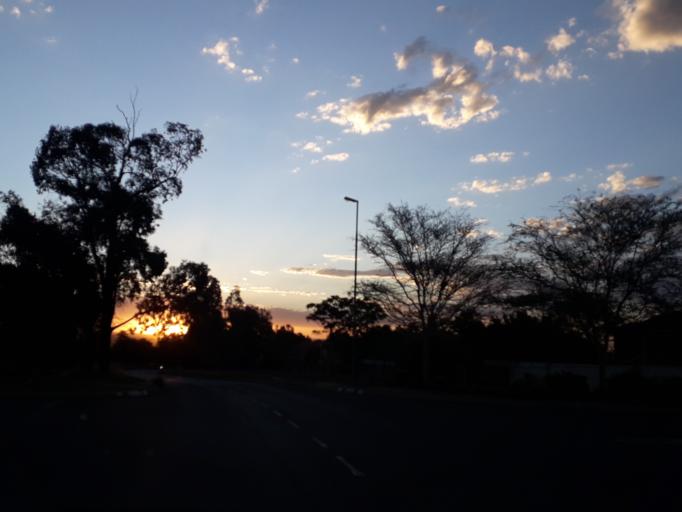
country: ZA
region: Gauteng
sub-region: City of Johannesburg Metropolitan Municipality
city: Midrand
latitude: -25.9950
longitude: 28.1030
